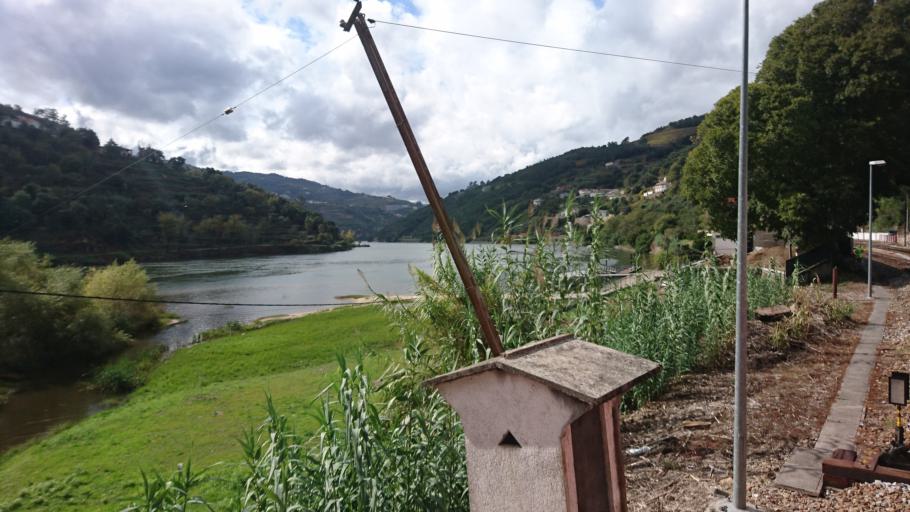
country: PT
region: Viseu
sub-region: Resende
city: Resende
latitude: 41.1246
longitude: -7.9483
